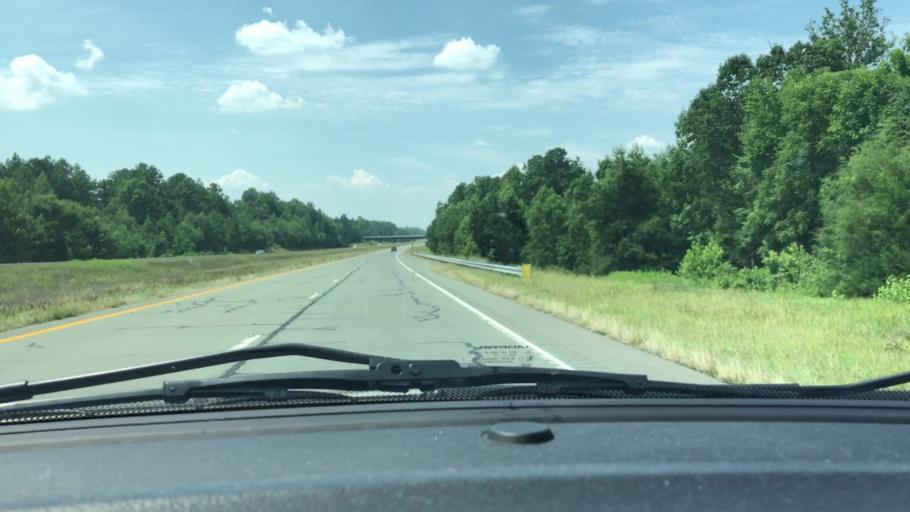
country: US
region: North Carolina
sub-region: Randolph County
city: Liberty
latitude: 35.7930
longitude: -79.5295
